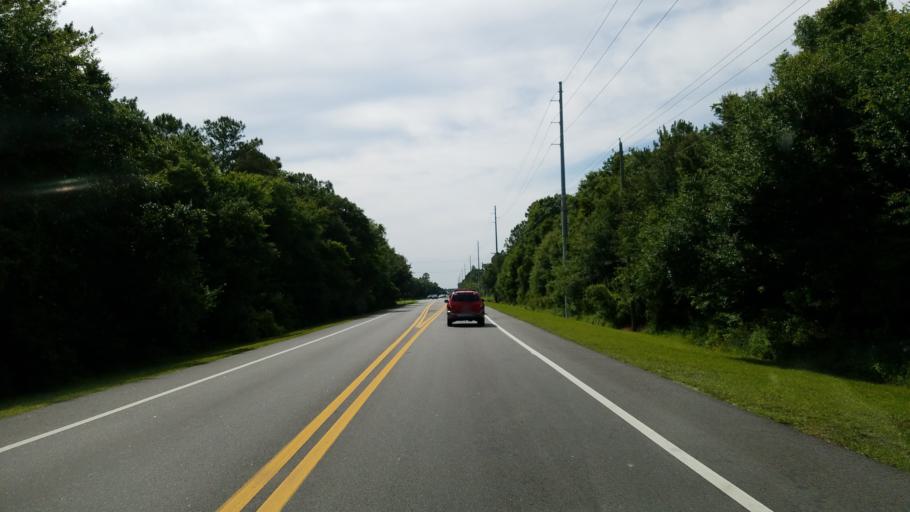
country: US
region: Florida
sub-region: Hillsborough County
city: Fish Hawk
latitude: 27.8560
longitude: -82.1904
